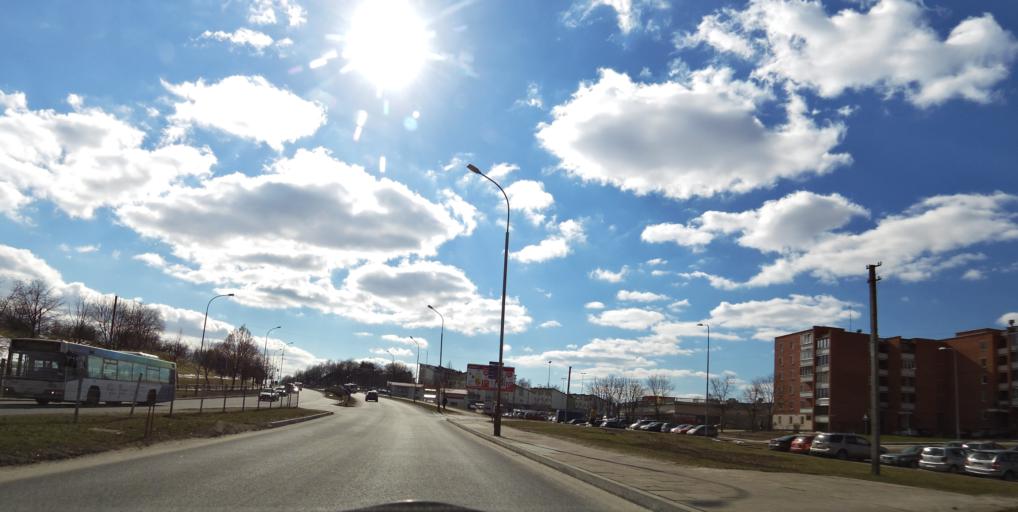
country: LT
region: Vilnius County
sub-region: Vilnius
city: Fabijoniskes
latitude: 54.7413
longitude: 25.2764
